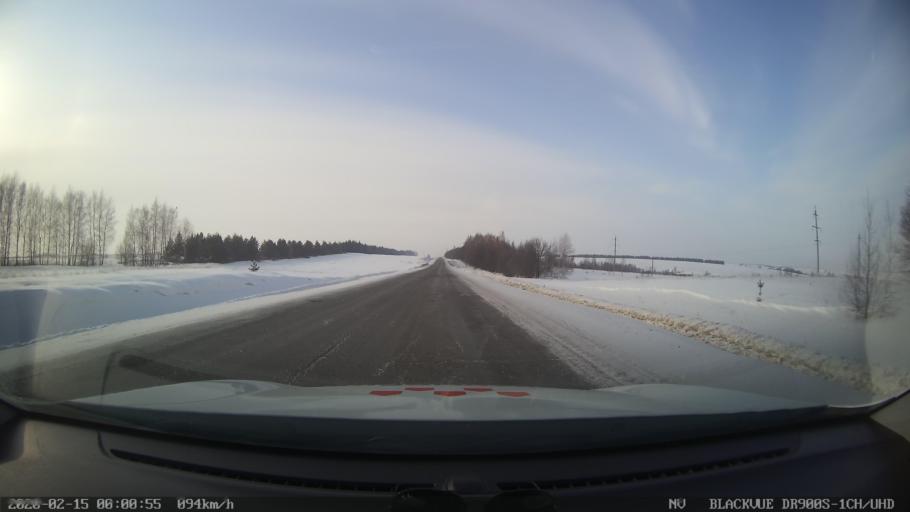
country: RU
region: Tatarstan
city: Kuybyshevskiy Zaton
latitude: 55.3447
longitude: 49.0274
